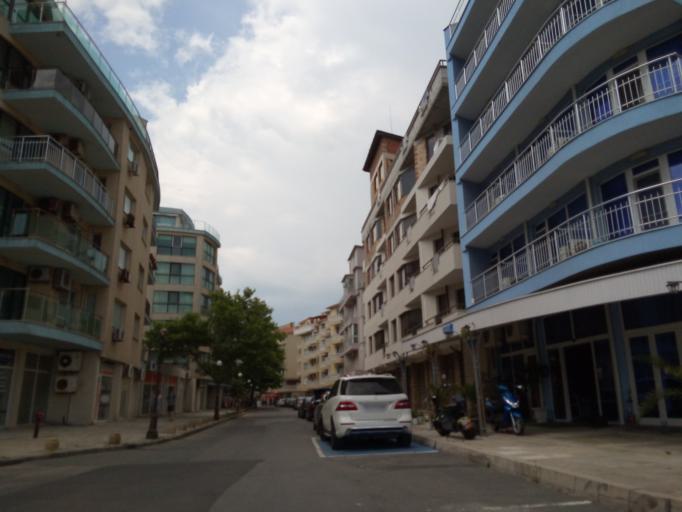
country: BG
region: Burgas
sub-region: Obshtina Pomorie
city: Pomorie
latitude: 42.5593
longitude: 27.6453
